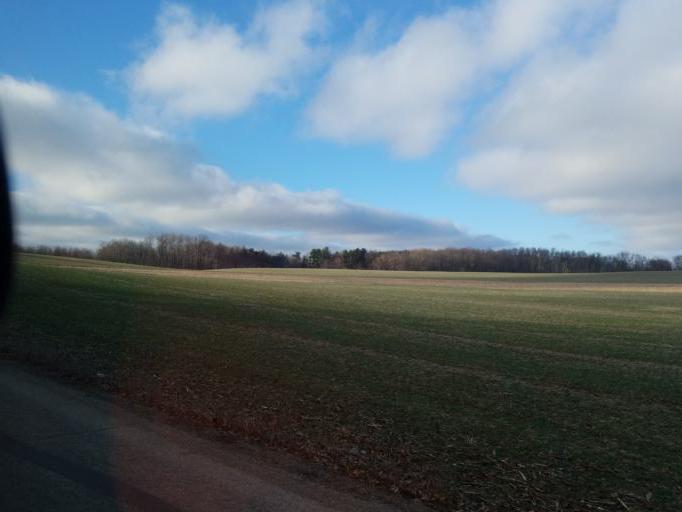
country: US
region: Ohio
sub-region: Ashland County
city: Loudonville
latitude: 40.6091
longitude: -82.3662
